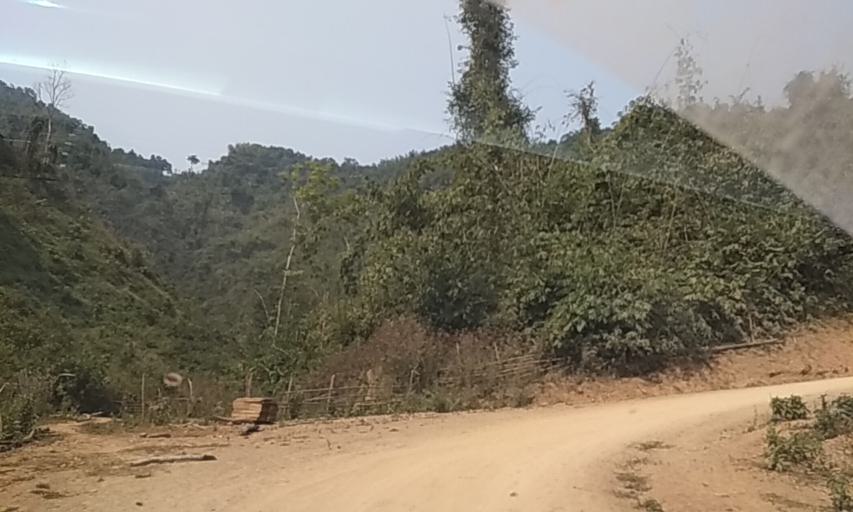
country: LA
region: Phongsali
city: Phongsali
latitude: 21.4683
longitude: 102.4321
